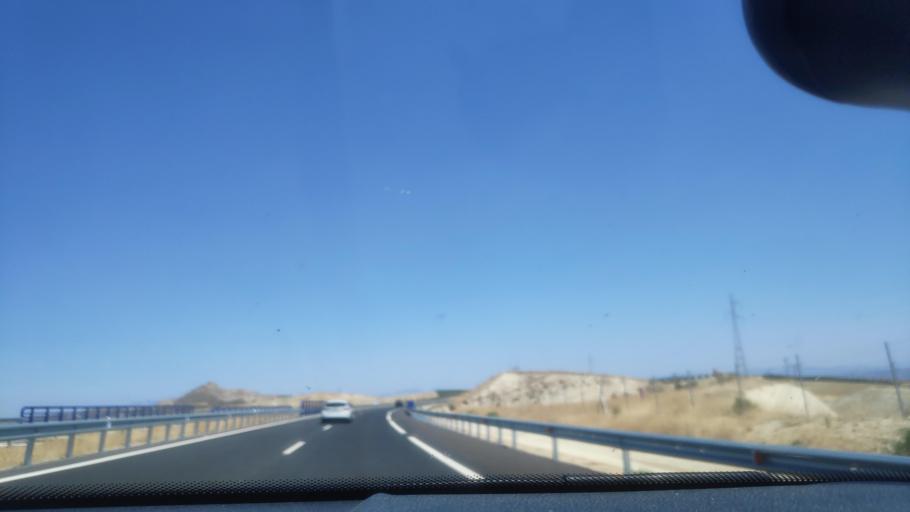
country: ES
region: Andalusia
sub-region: Provincia de Granada
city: Otura
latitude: 37.0754
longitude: -3.6621
